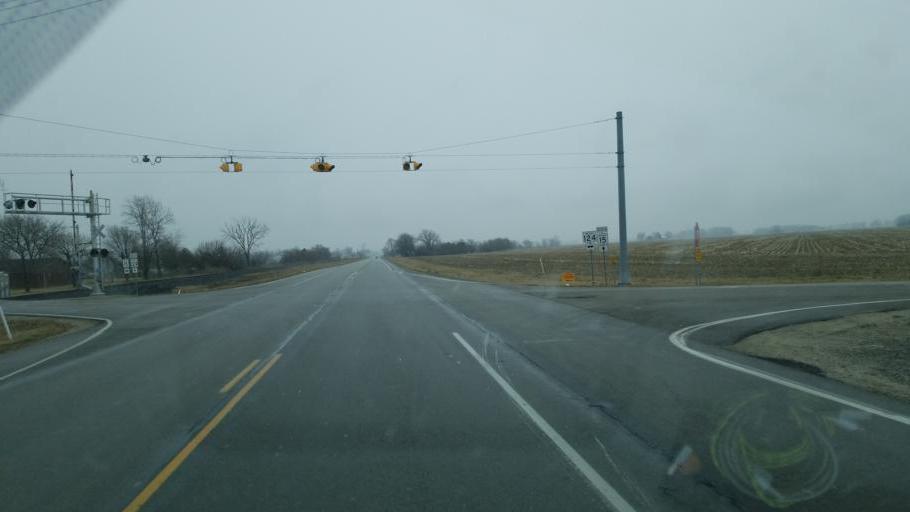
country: US
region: Indiana
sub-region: Wabash County
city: Wabash
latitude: 40.7391
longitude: -85.7944
